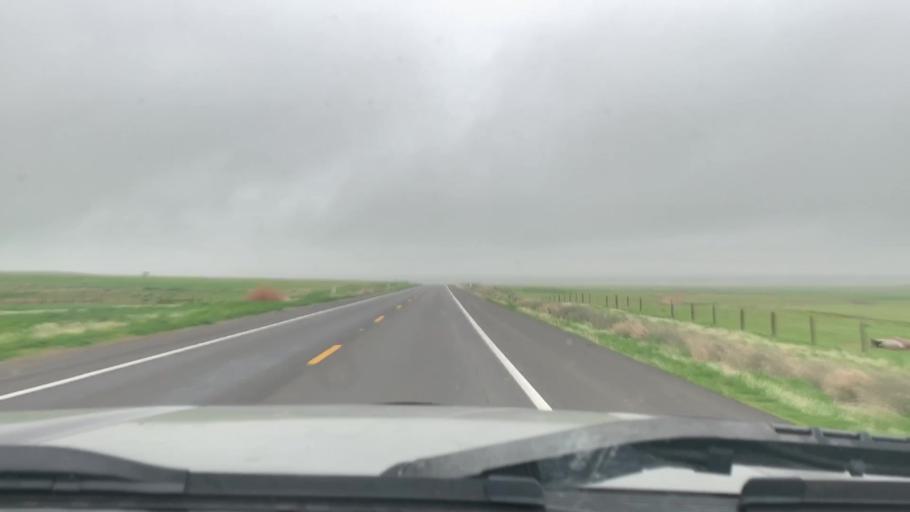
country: US
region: California
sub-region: Kings County
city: Avenal
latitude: 35.7813
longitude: -120.1261
